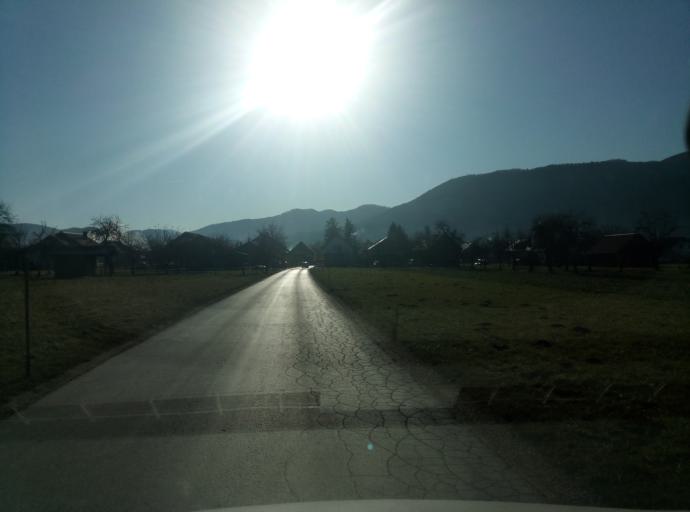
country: SI
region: Cerknica
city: Cerknica
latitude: 45.7791
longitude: 14.3591
